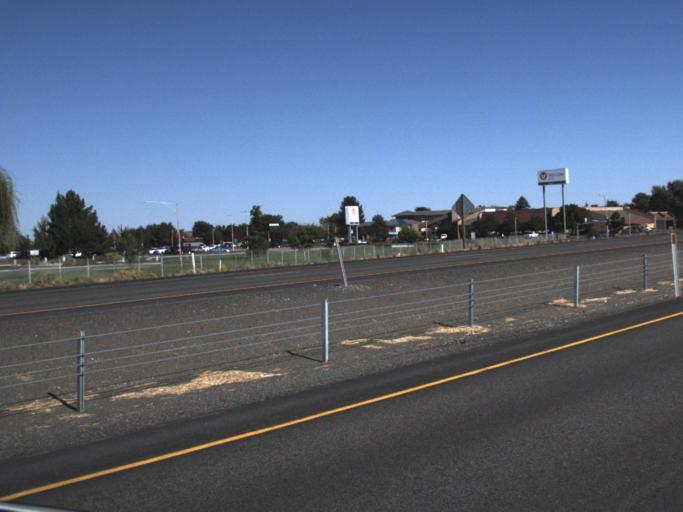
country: US
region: Washington
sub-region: Franklin County
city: Pasco
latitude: 46.2486
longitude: -119.1195
